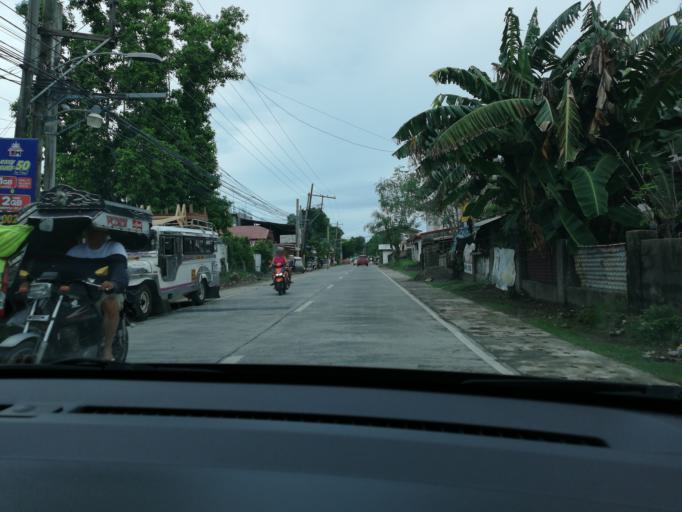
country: PH
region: Ilocos
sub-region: Province of Ilocos Sur
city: Bantay
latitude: 17.5831
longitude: 120.3851
